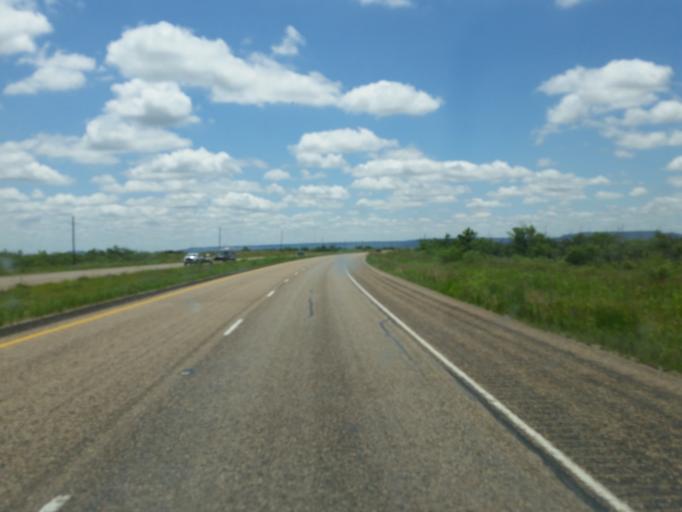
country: US
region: Texas
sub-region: Garza County
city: Post
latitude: 33.0901
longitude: -101.2451
